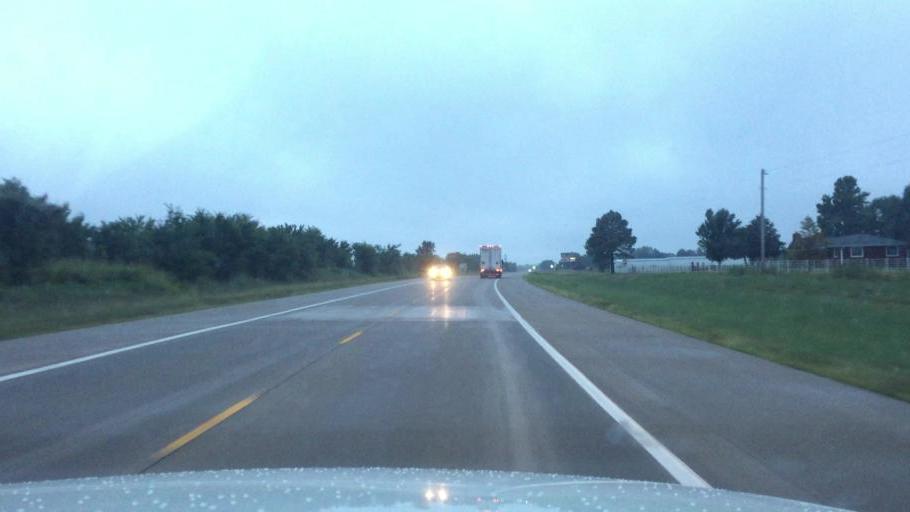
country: US
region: Kansas
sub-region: Neosho County
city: Chanute
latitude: 37.5021
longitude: -95.4706
